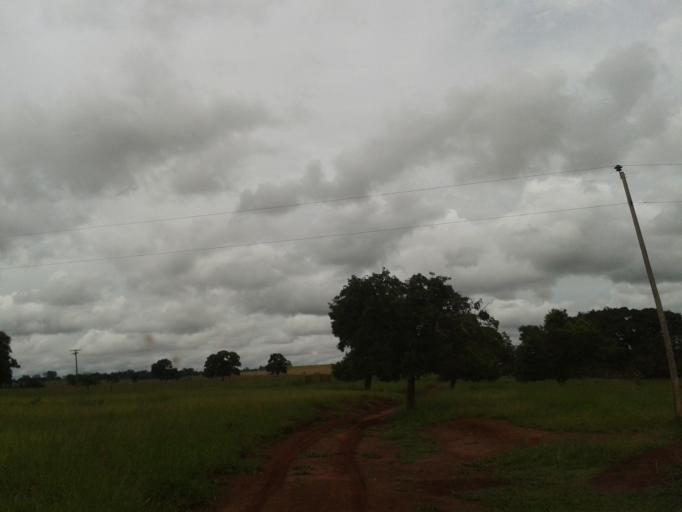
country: BR
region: Minas Gerais
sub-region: Capinopolis
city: Capinopolis
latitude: -18.7818
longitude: -49.7838
